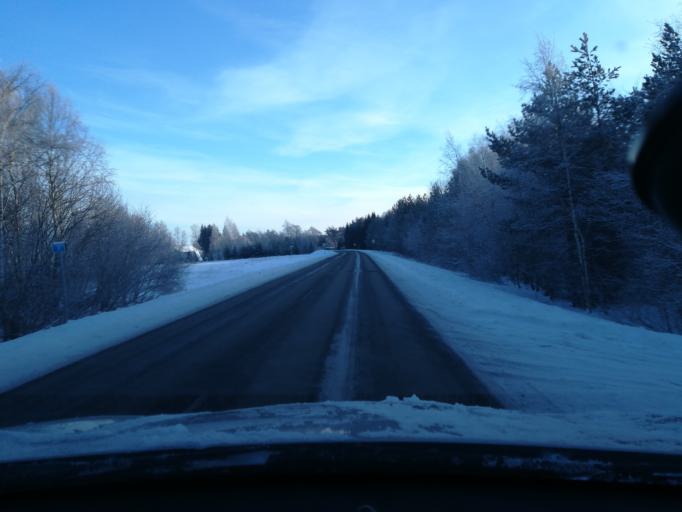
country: EE
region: Harju
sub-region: Keila linn
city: Keila
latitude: 59.3780
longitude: 24.4574
